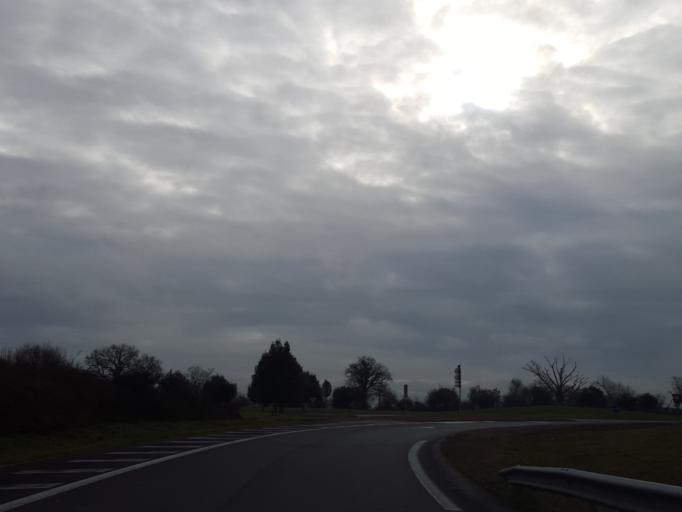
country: FR
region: Pays de la Loire
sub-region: Departement de la Vendee
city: La Chaize-le-Vicomte
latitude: 46.6691
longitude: -1.3157
